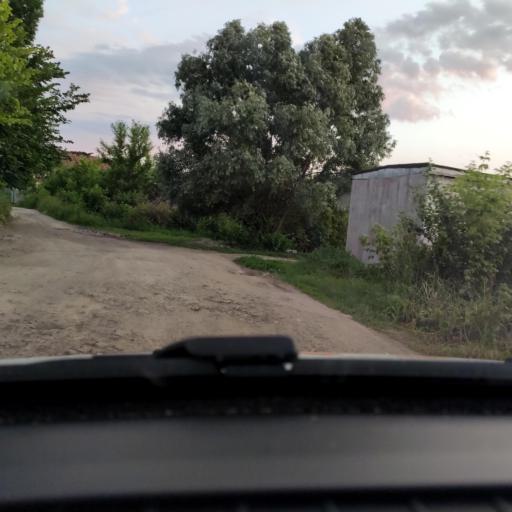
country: RU
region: Voronezj
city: Semiluki
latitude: 51.7442
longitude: 39.0176
